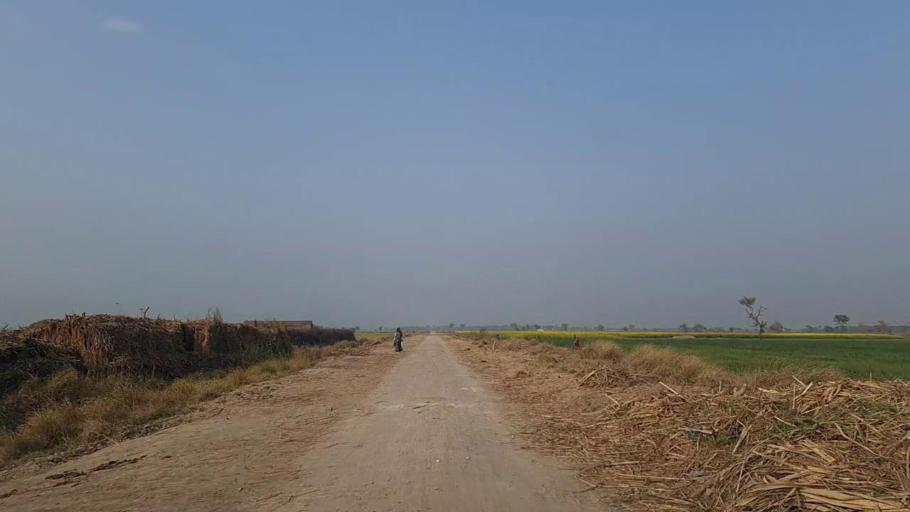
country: PK
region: Sindh
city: Jam Sahib
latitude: 26.3343
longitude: 68.5147
